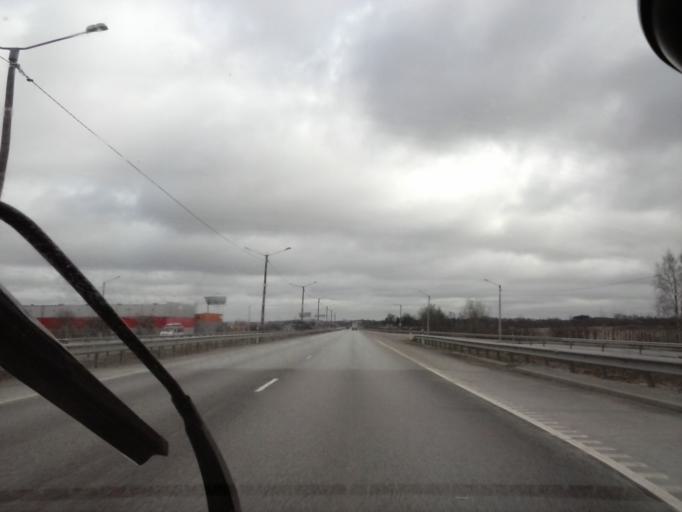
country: EE
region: Harju
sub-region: Rae vald
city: Jueri
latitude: 59.3509
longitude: 24.8859
